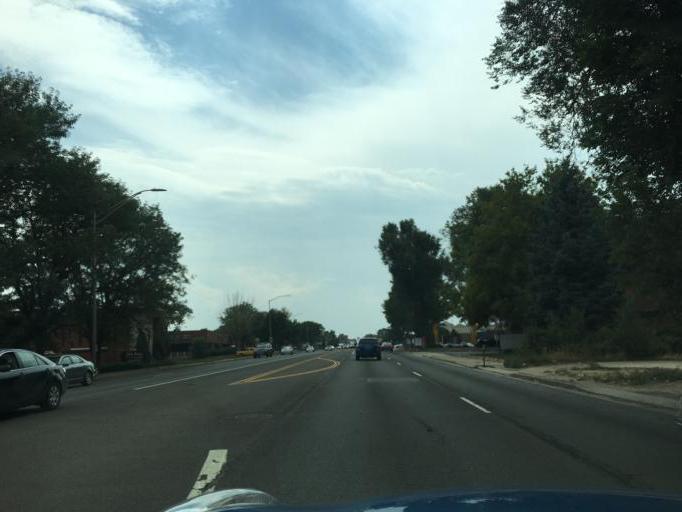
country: US
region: Colorado
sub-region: Jefferson County
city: Wheat Ridge
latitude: 39.7796
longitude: -105.0815
